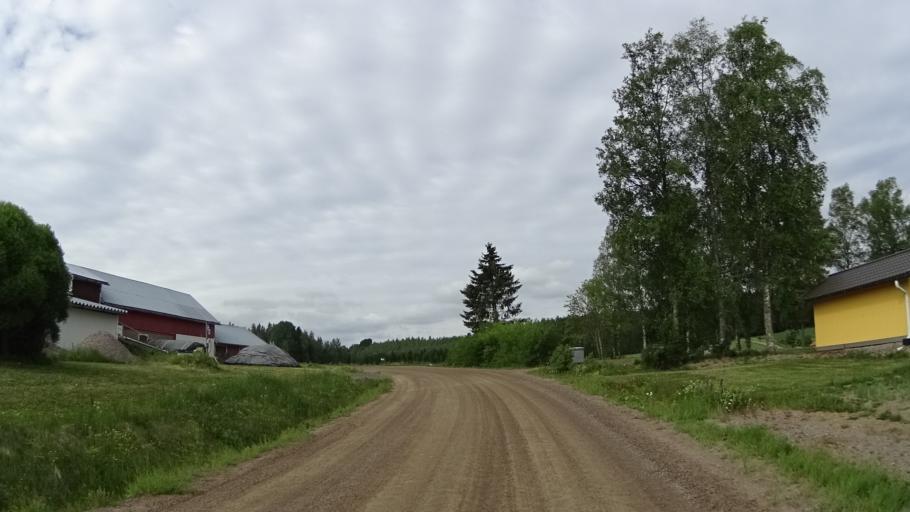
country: FI
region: Uusimaa
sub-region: Helsinki
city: Karkkila
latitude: 60.4805
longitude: 24.2613
